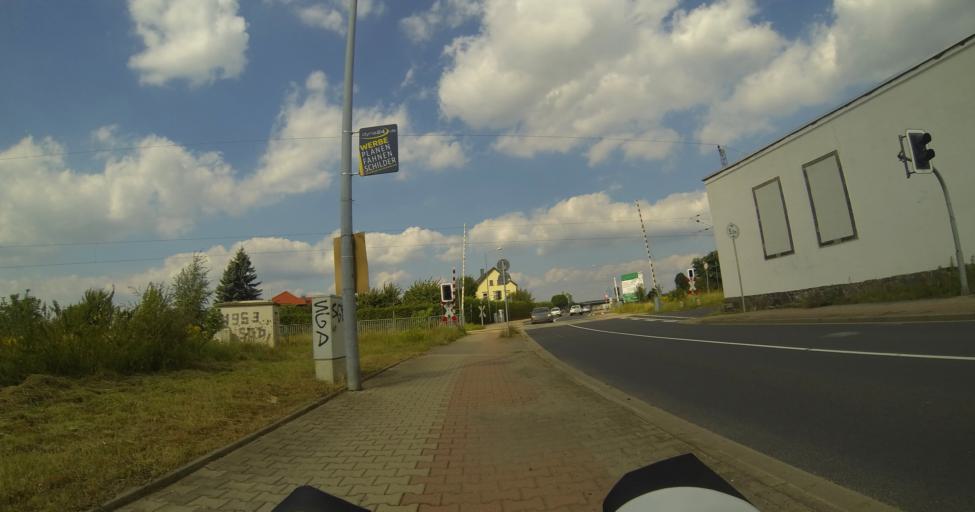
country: DE
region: Saxony
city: Grossenhain
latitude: 51.2991
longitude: 13.5339
